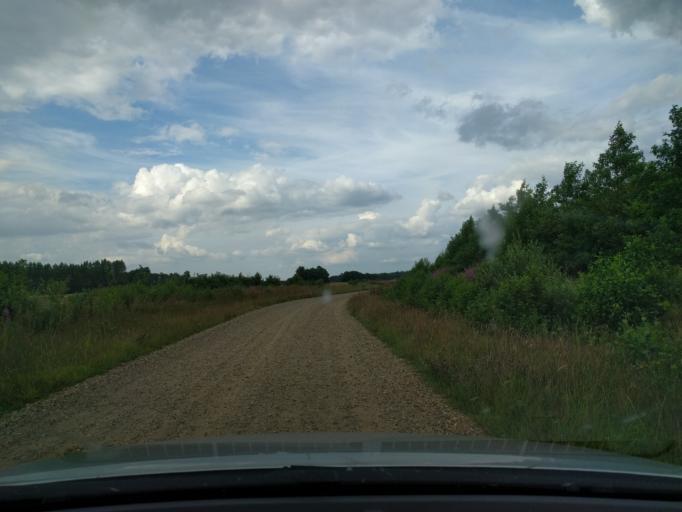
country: DK
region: Central Jutland
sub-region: Herning Kommune
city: Kibaek
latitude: 56.0693
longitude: 8.8850
